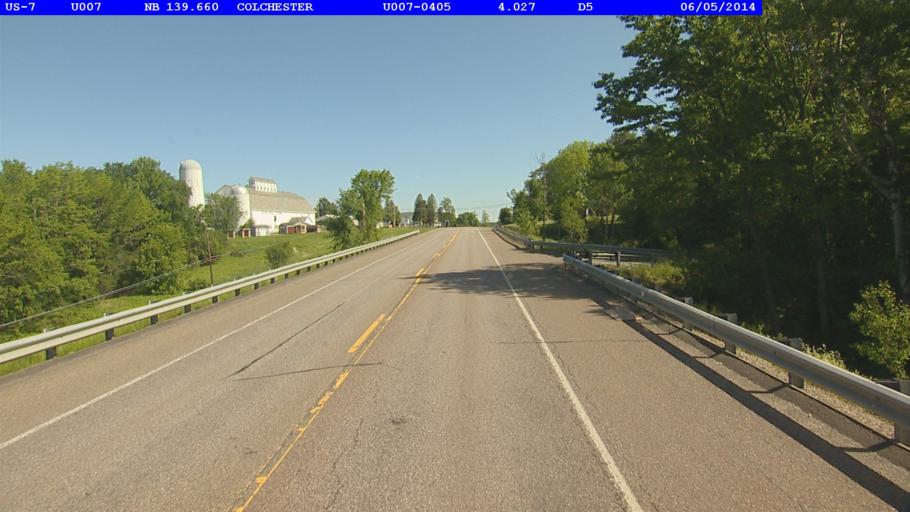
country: US
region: Vermont
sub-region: Chittenden County
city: Colchester
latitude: 44.5567
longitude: -73.1622
